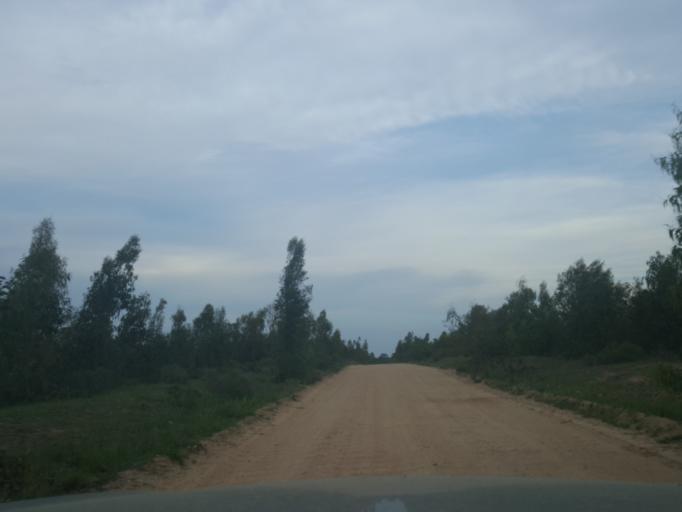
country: ZA
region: Limpopo
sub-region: Mopani District Municipality
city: Hoedspruit
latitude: -24.5876
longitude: 30.9657
